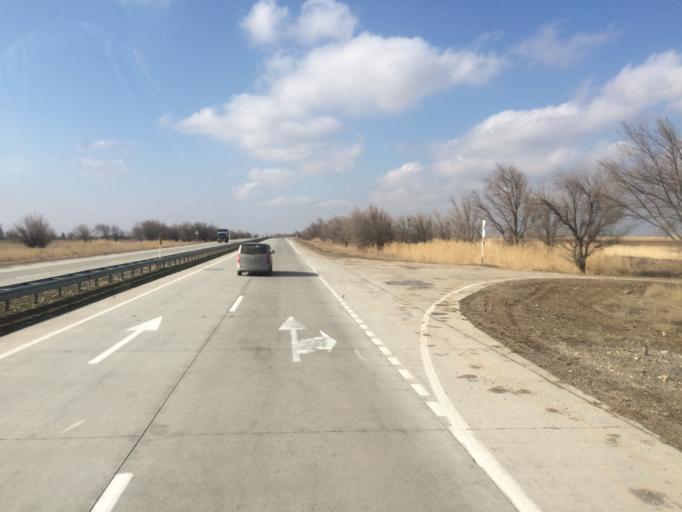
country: KZ
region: Ongtustik Qazaqstan
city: Bayaldyr
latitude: 43.0084
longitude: 68.7744
